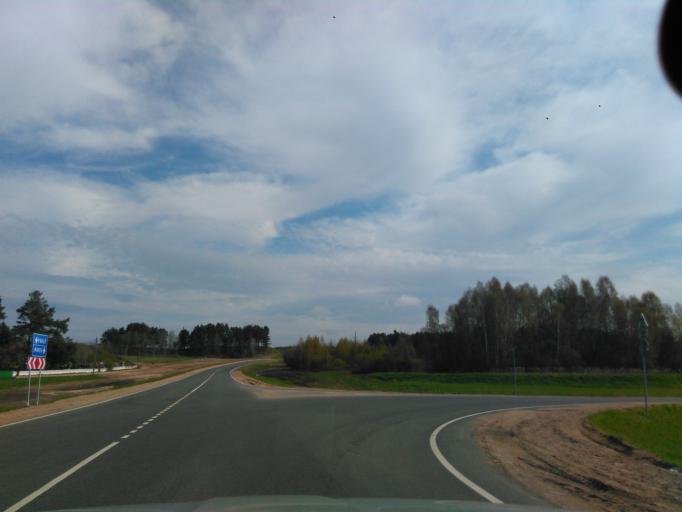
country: BY
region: Minsk
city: Rakaw
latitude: 53.9672
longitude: 27.0743
